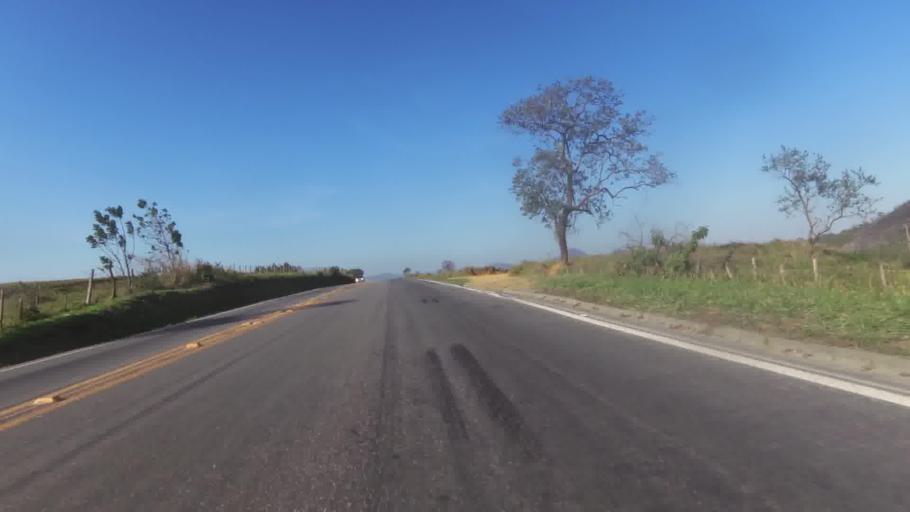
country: BR
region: Espirito Santo
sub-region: Alfredo Chaves
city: Alfredo Chaves
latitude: -20.6971
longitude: -40.7105
